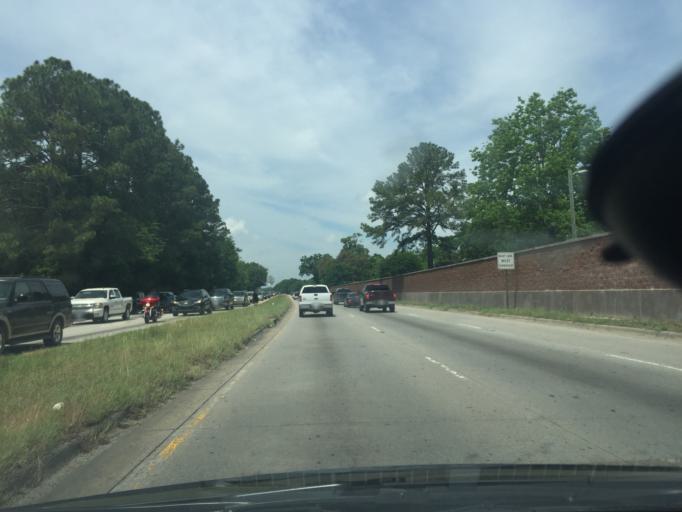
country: US
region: Georgia
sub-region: Chatham County
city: Savannah
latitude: 32.0306
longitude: -81.1163
